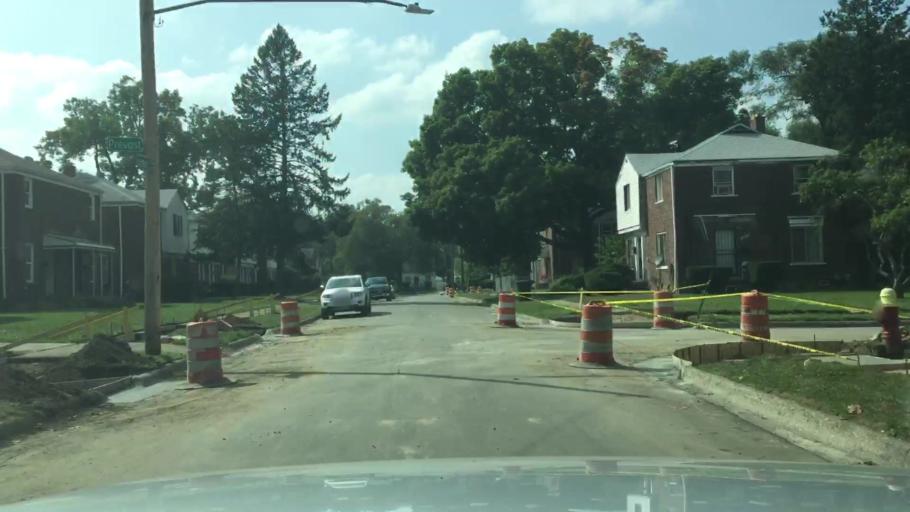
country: US
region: Michigan
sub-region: Wayne County
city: Dearborn
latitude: 42.3591
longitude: -83.2011
